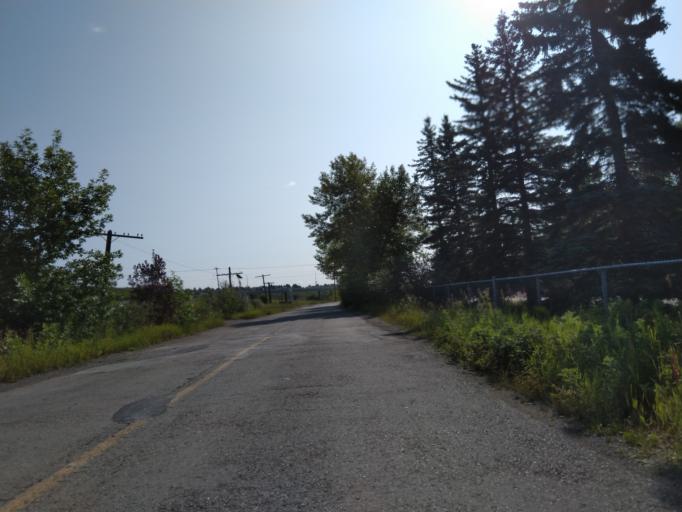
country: CA
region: Alberta
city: Calgary
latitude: 51.1014
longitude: -114.2136
